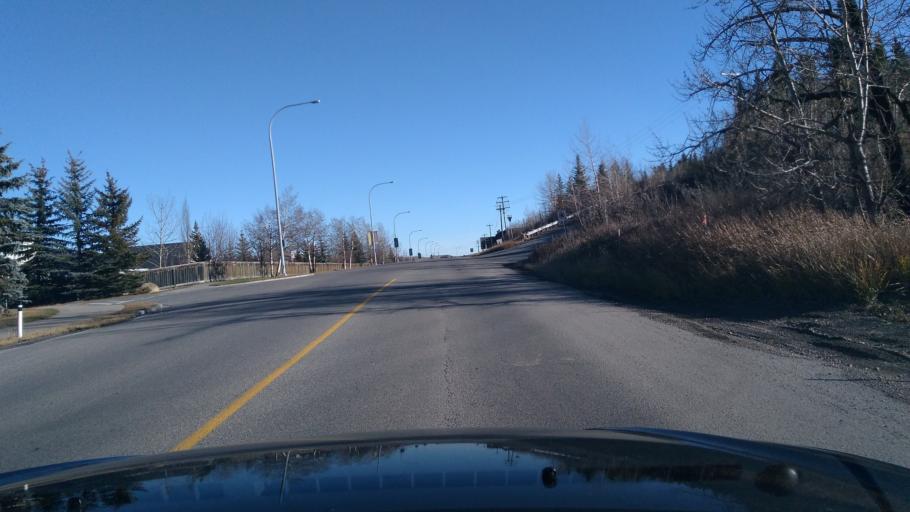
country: CA
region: Alberta
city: Cochrane
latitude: 51.1840
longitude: -114.4983
